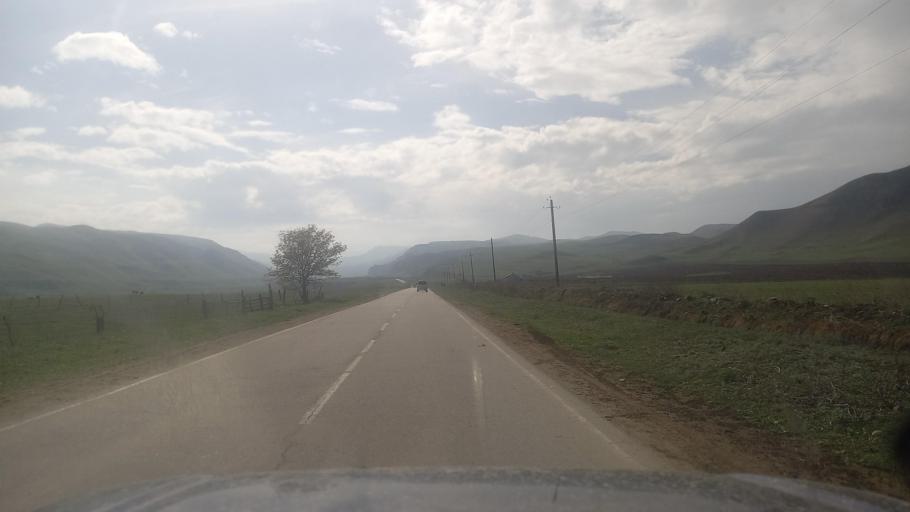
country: RU
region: Kabardino-Balkariya
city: Kamennomostskoye
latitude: 43.7360
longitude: 43.0084
